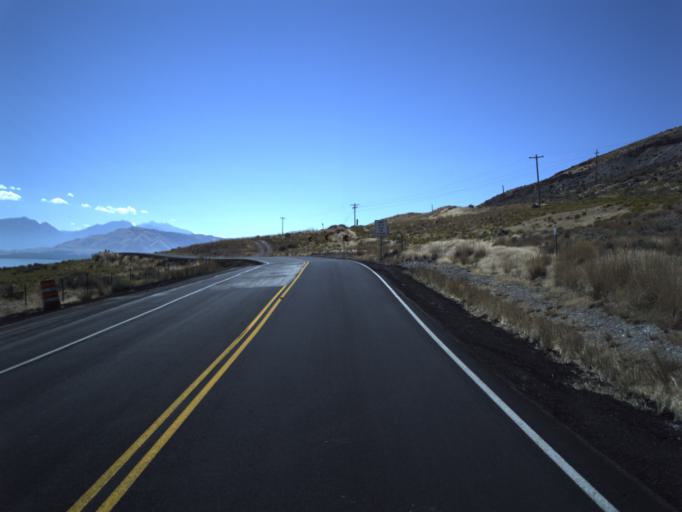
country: US
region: Utah
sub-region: Utah County
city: Saratoga Springs
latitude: 40.2542
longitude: -111.8671
